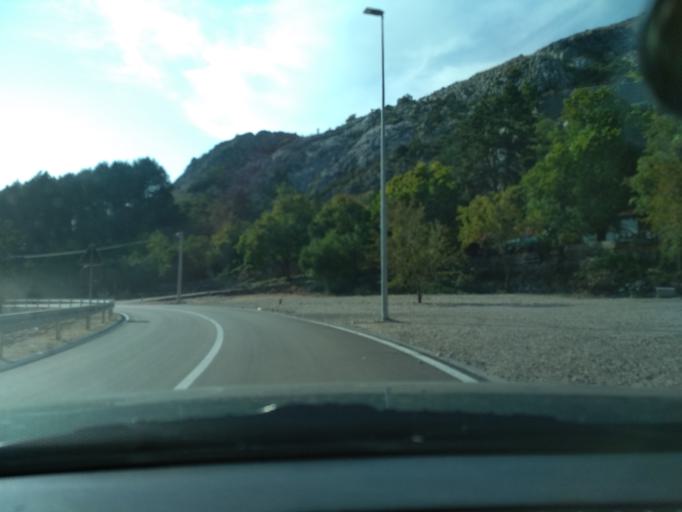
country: ME
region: Kotor
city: Kotor
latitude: 42.4355
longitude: 18.8473
